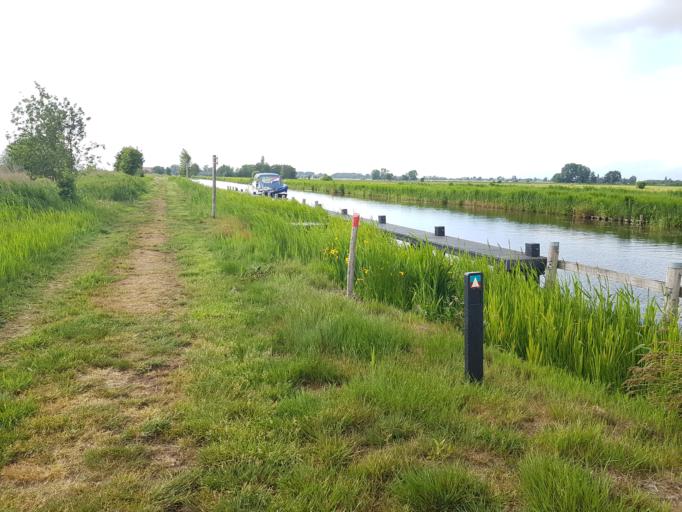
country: NL
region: Friesland
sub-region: Gemeente Smallingerland
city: Oudega
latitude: 53.0892
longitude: 5.9687
